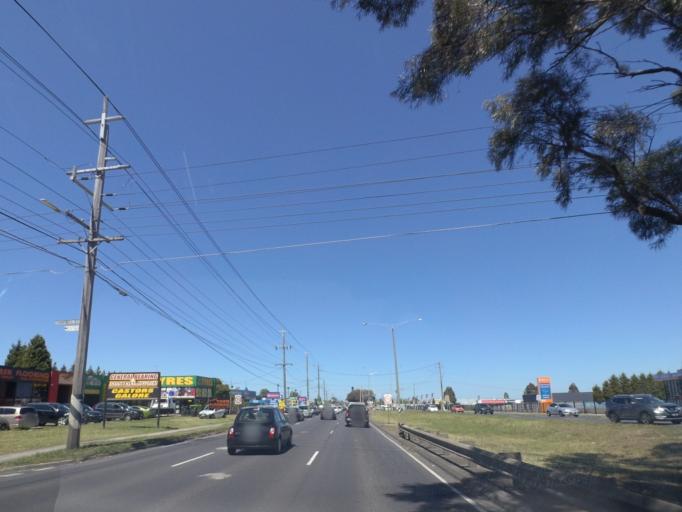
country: AU
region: Victoria
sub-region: Hume
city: Campbellfield
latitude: -37.6775
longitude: 144.9565
